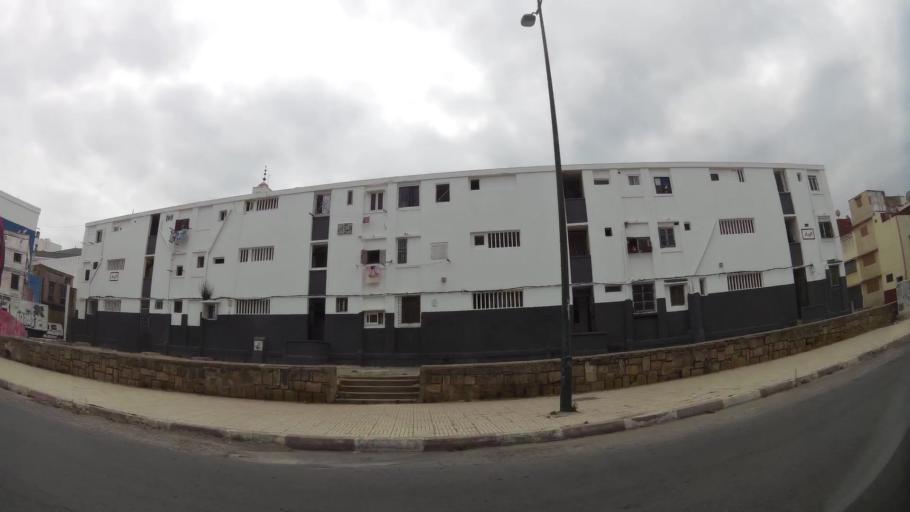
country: MA
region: Rabat-Sale-Zemmour-Zaer
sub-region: Rabat
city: Rabat
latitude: 33.9936
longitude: -6.8777
